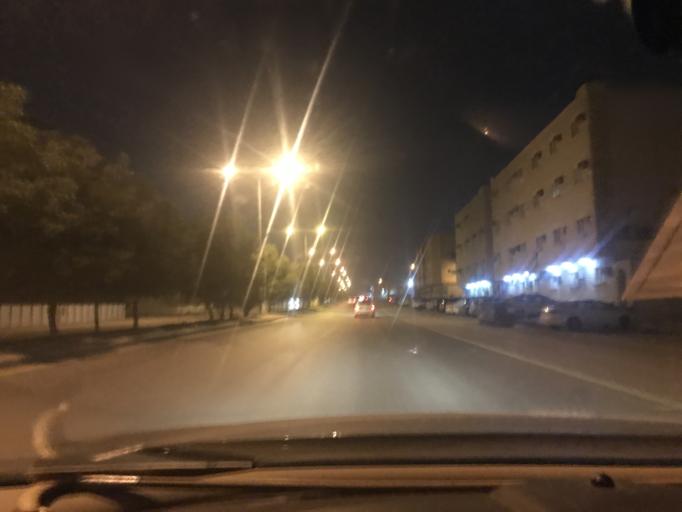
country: SA
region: Ar Riyad
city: Riyadh
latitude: 24.7504
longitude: 46.7540
